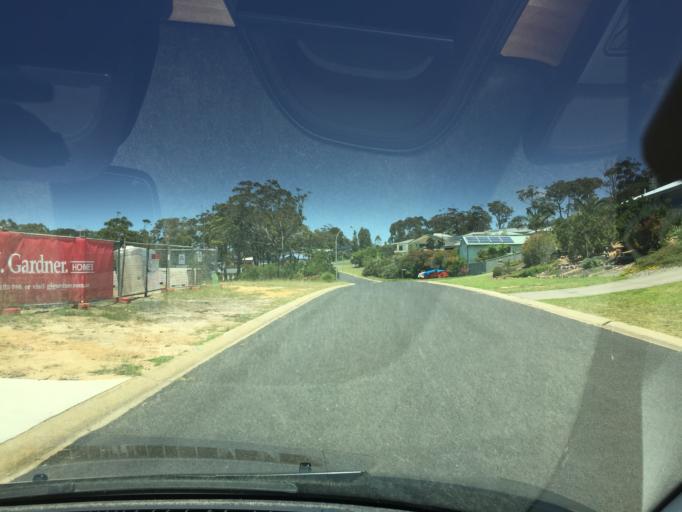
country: AU
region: New South Wales
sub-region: Bega Valley
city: Merimbula
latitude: -36.8489
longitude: 149.9272
